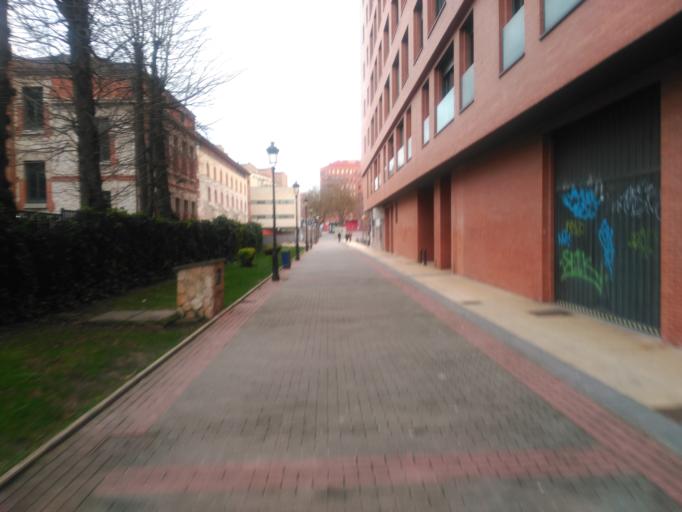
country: ES
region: Castille and Leon
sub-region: Provincia de Burgos
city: Burgos
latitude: 42.3348
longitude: -3.7010
